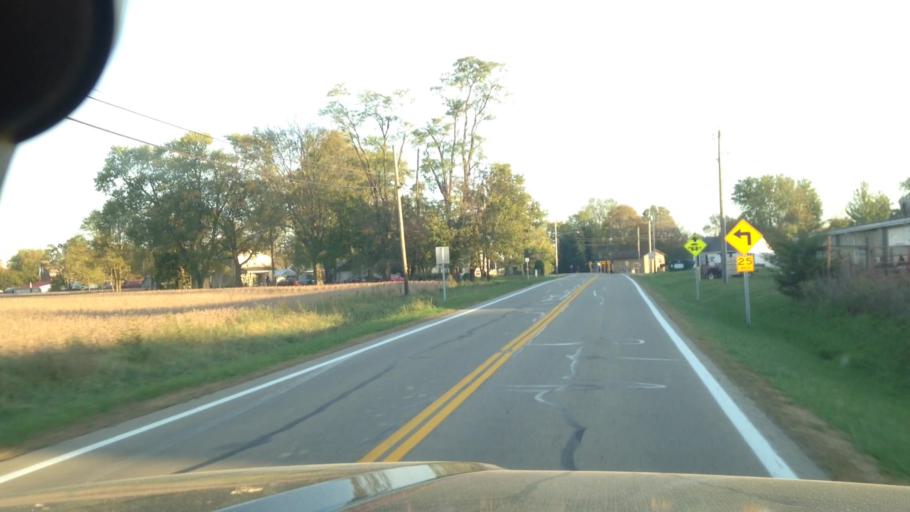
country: US
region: Ohio
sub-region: Butler County
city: Oxford
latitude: 39.5978
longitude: -84.7397
